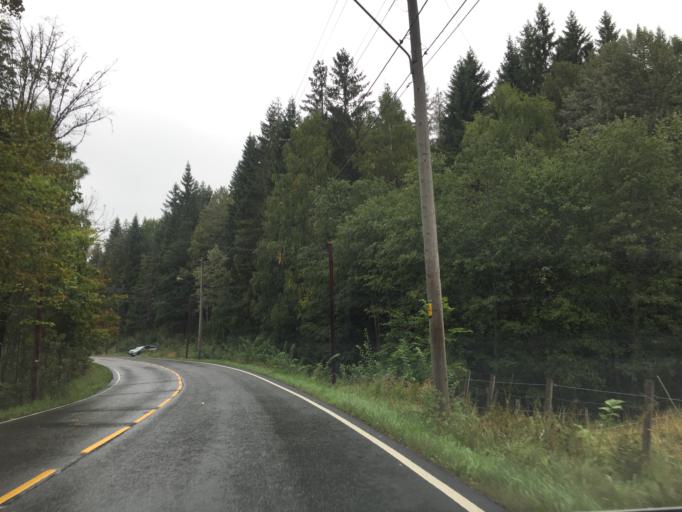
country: NO
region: Akershus
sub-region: Baerum
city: Lysaker
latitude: 59.9744
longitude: 10.6263
